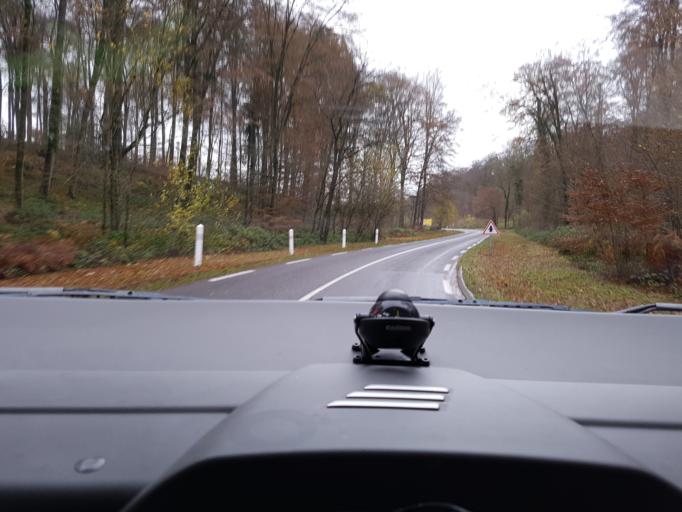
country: FR
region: Haute-Normandie
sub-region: Departement de l'Eure
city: Etrepagny
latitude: 49.4166
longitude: 1.6323
